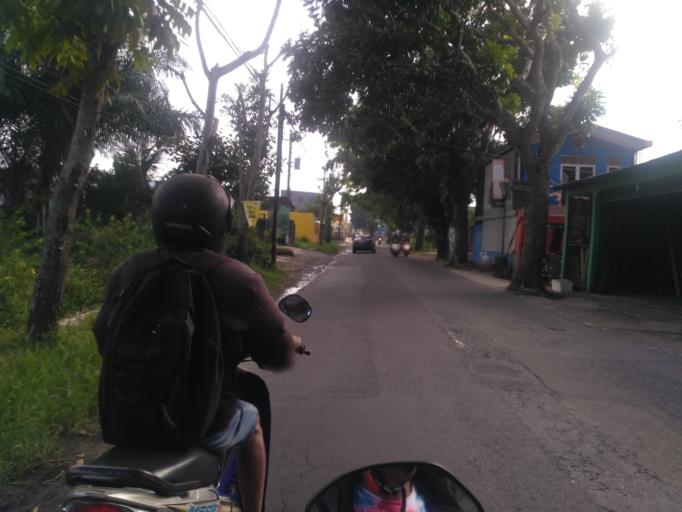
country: ID
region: Daerah Istimewa Yogyakarta
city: Yogyakarta
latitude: -7.7599
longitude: 110.3458
